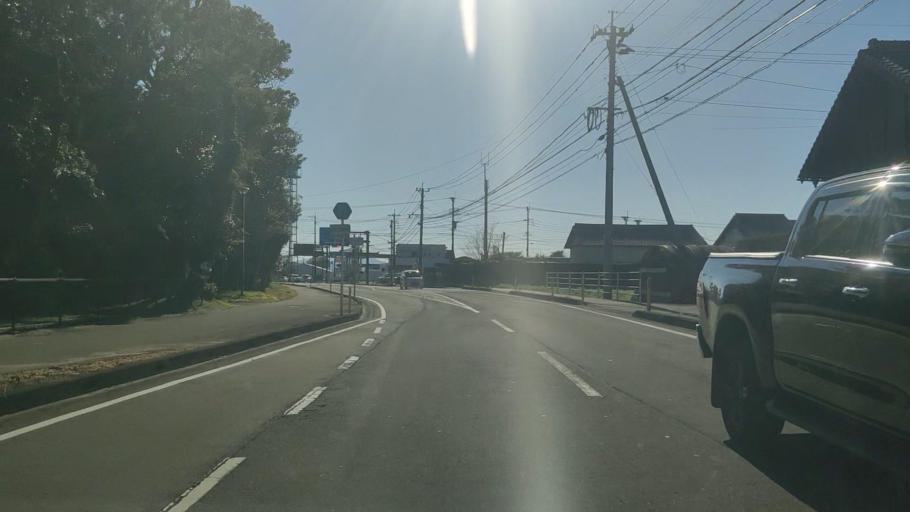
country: JP
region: Miyazaki
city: Miyazaki-shi
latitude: 31.9575
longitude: 131.4632
